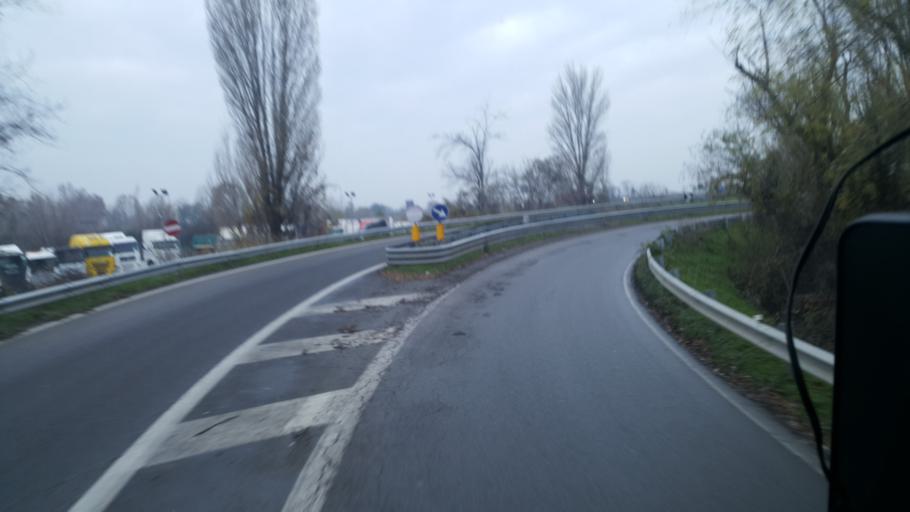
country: IT
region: Emilia-Romagna
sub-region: Provincia di Parma
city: Parma
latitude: 44.8208
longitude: 10.3124
